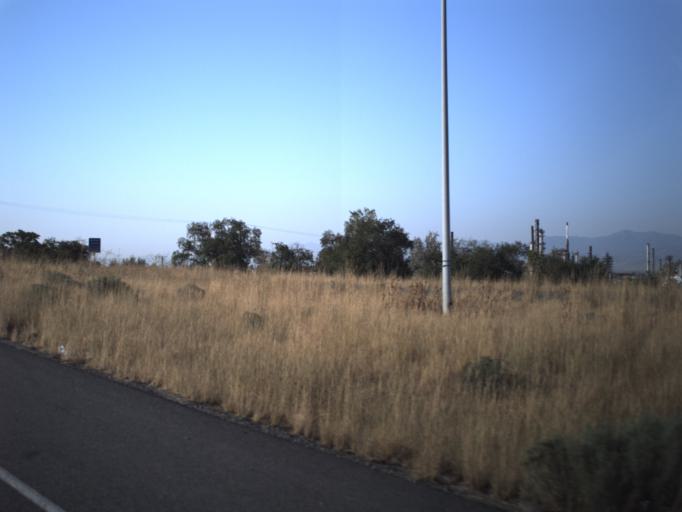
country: US
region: Utah
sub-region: Davis County
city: North Salt Lake
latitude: 40.8293
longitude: -111.9167
